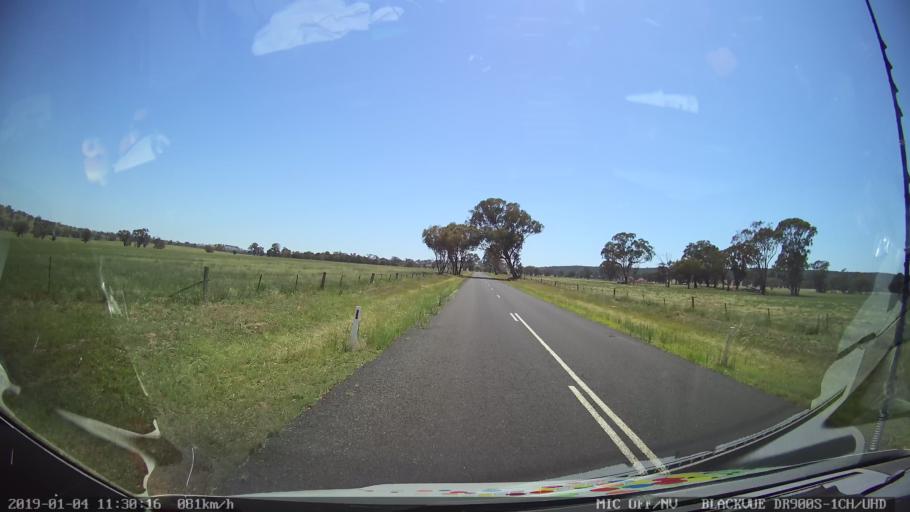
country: AU
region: New South Wales
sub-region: Cabonne
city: Molong
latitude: -33.0791
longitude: 148.7793
